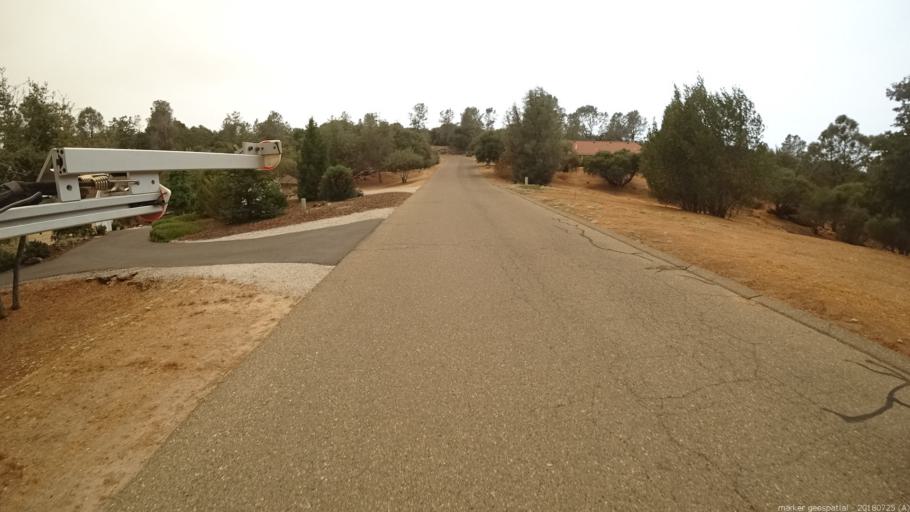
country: US
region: California
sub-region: Madera County
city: Coarsegold
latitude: 37.1989
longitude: -119.6842
